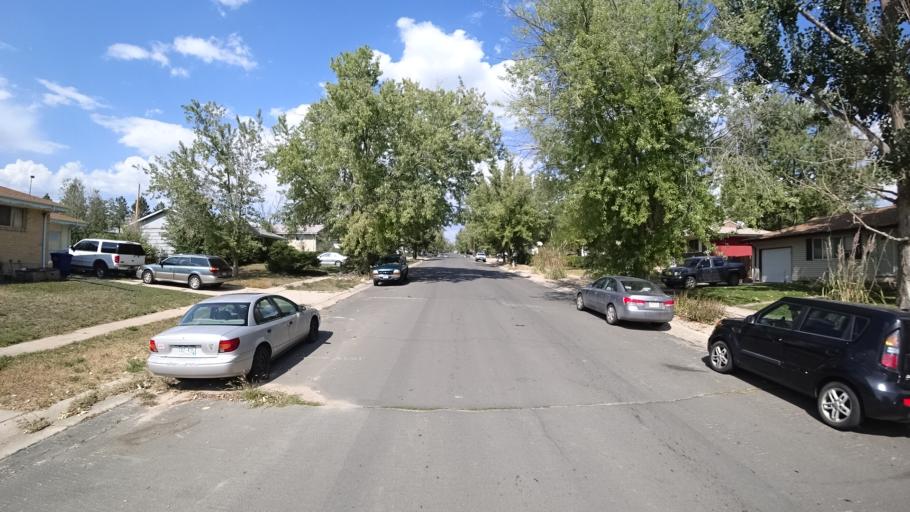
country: US
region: Colorado
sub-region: El Paso County
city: Colorado Springs
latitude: 38.8480
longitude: -104.7707
